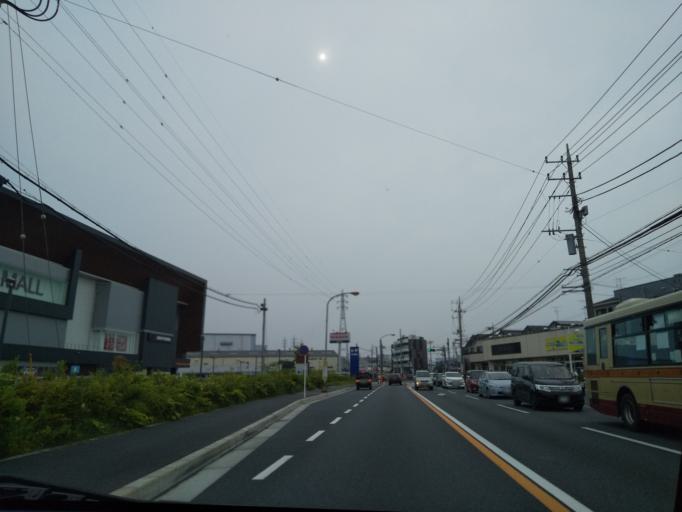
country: JP
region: Kanagawa
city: Minami-rinkan
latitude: 35.5021
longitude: 139.4263
